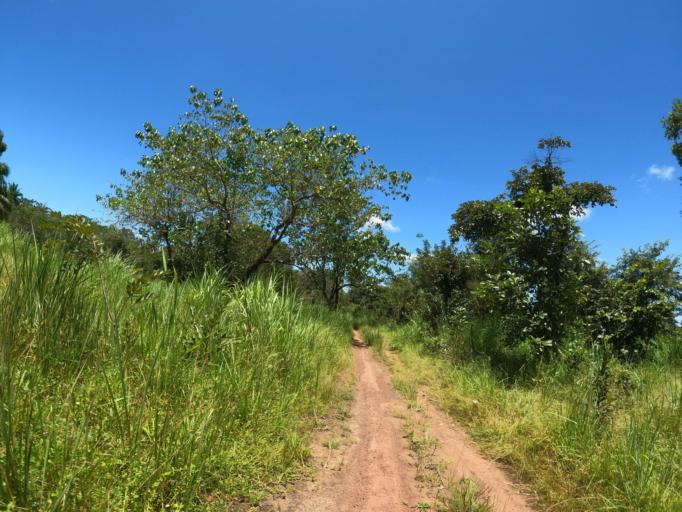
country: SL
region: Northern Province
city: Makeni
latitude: 9.1048
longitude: -12.2508
